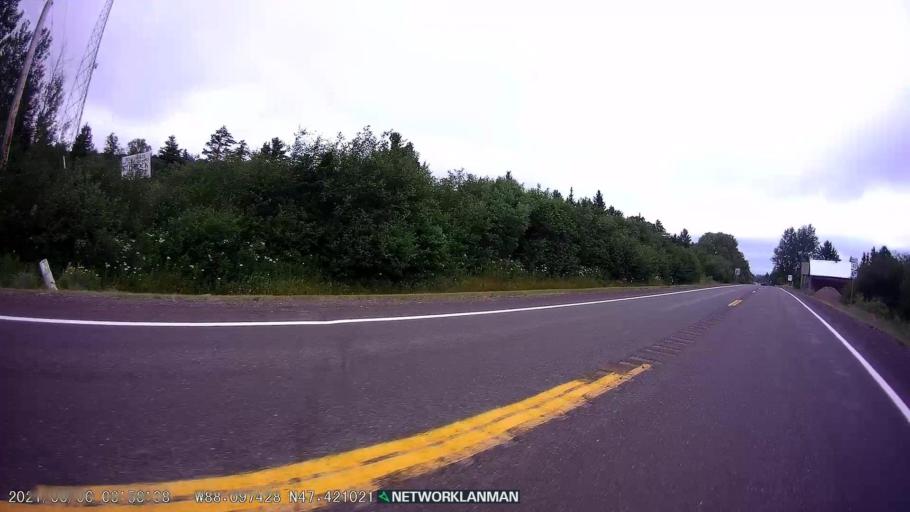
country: US
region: Michigan
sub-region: Keweenaw County
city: Eagle River
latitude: 47.4210
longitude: -88.0970
